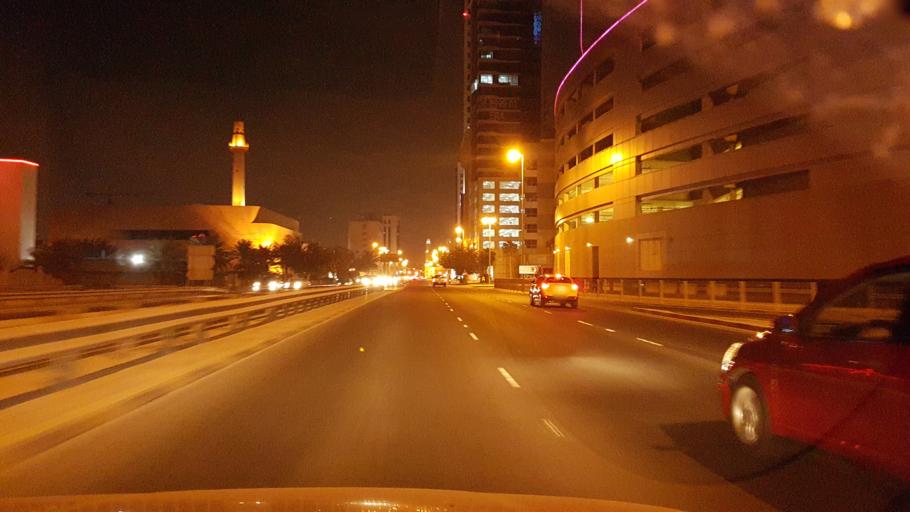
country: BH
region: Muharraq
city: Al Muharraq
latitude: 26.2412
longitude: 50.5928
